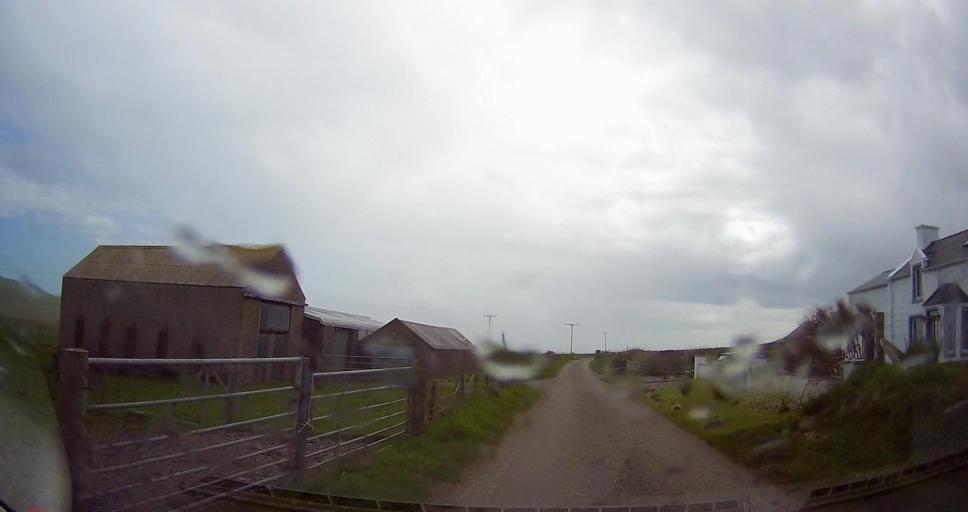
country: GB
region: Scotland
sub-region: Shetland Islands
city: Sandwick
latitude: 59.9076
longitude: -1.3345
